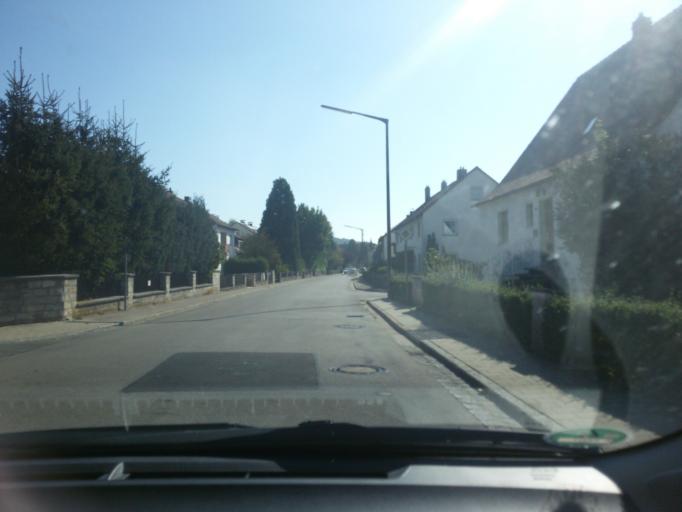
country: DE
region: Bavaria
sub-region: Regierungsbezirk Mittelfranken
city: Wassertrudingen
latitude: 49.0445
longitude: 10.6010
